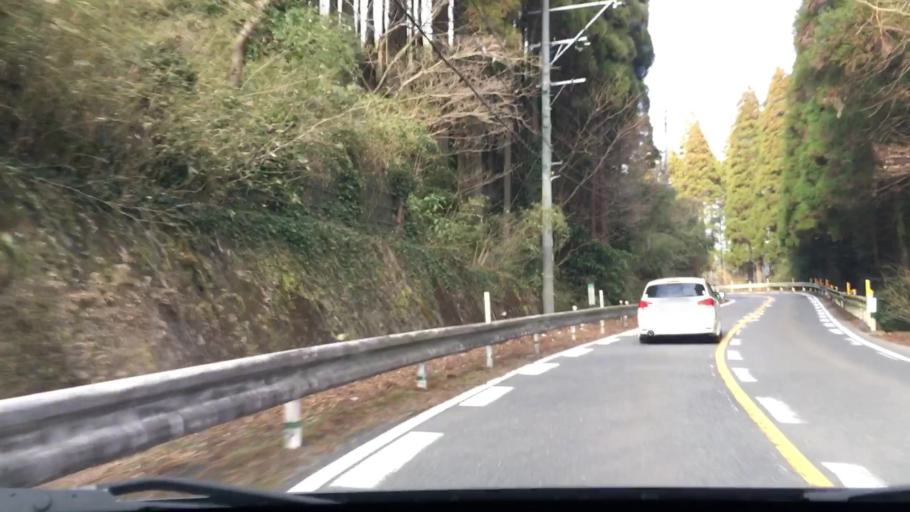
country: JP
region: Miyazaki
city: Nichinan
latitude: 31.7302
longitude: 131.3305
